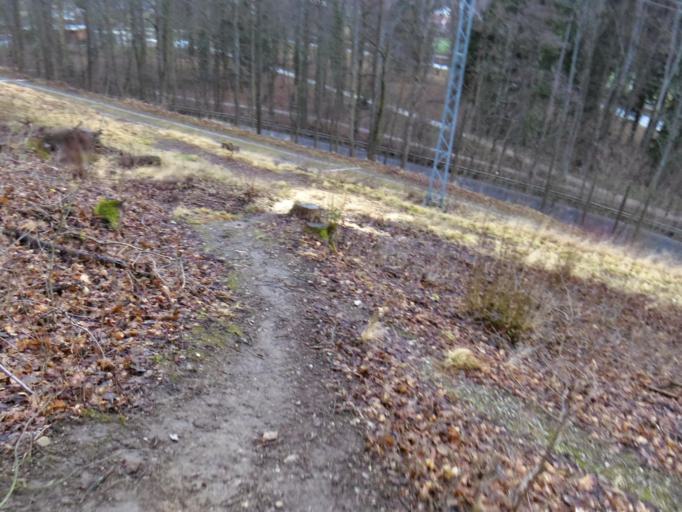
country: CZ
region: Plzensky
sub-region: Okres Klatovy
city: Susice
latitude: 49.2255
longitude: 13.5183
